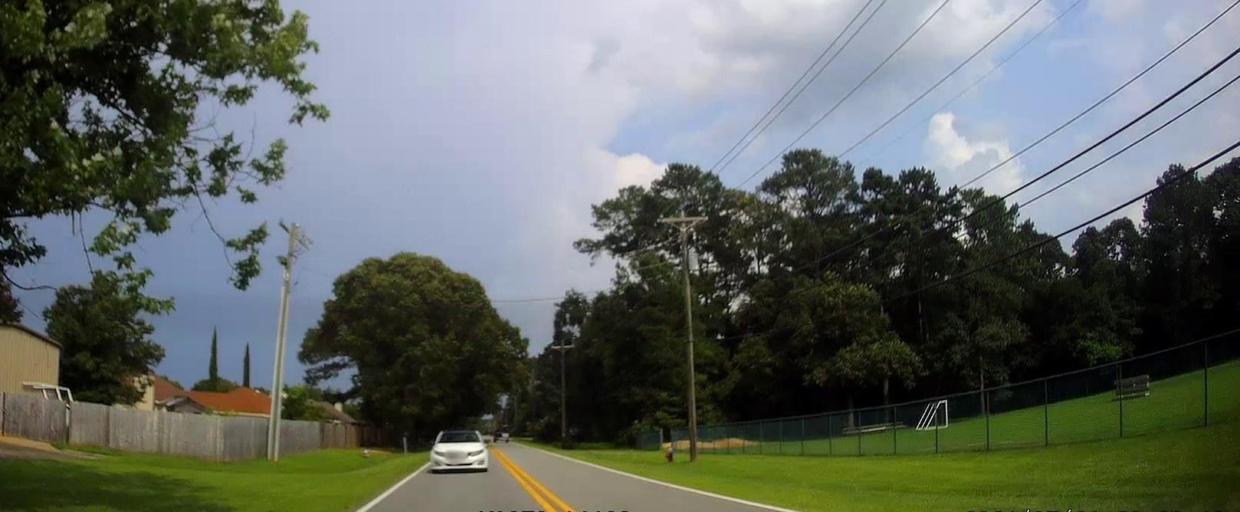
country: US
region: Georgia
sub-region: Houston County
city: Warner Robins
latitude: 32.5778
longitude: -83.6215
